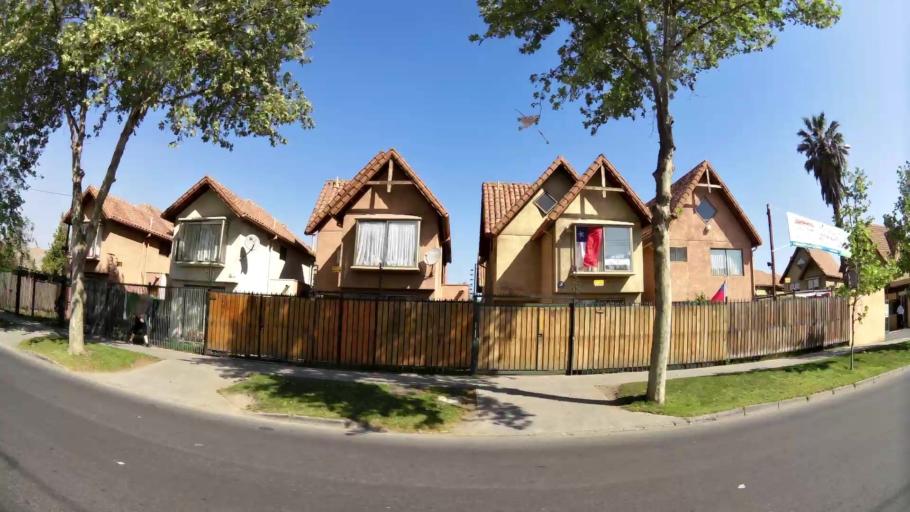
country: CL
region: Santiago Metropolitan
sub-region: Provincia de Santiago
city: La Pintana
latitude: -33.5395
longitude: -70.5943
